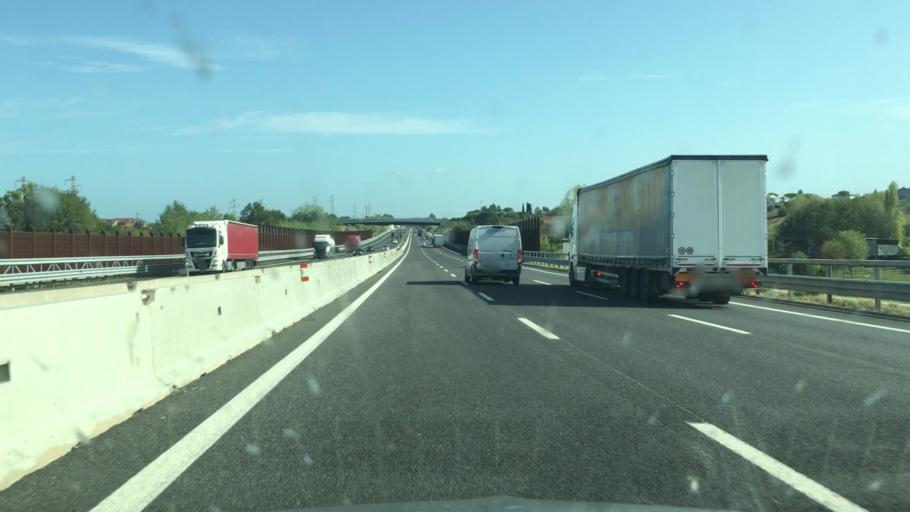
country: IT
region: Emilia-Romagna
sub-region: Provincia di Rimini
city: Rivazzurra
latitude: 44.0144
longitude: 12.5897
